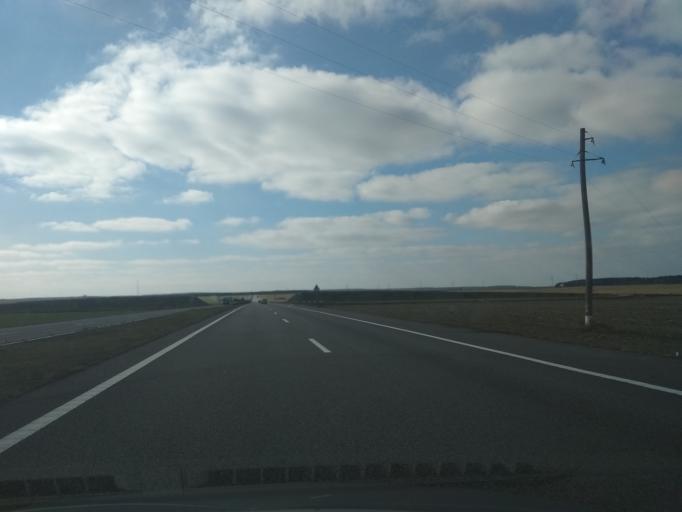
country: BY
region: Minsk
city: Haradzyeya
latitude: 53.4085
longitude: 26.5597
